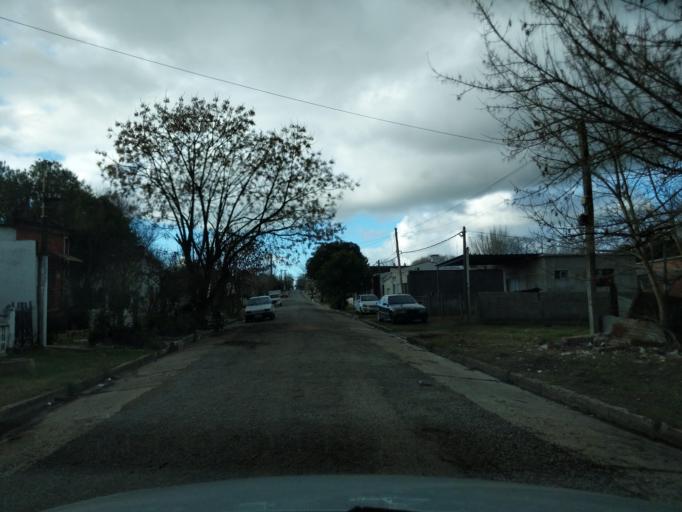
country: UY
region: Florida
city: Florida
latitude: -34.1051
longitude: -56.2217
